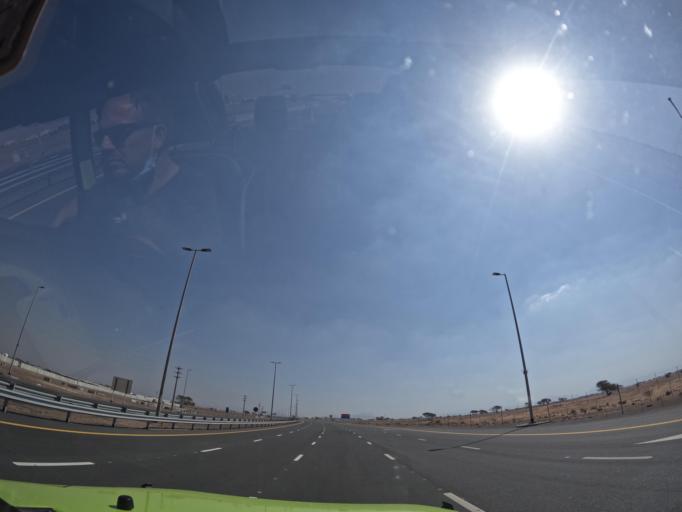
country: AE
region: Ash Shariqah
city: Adh Dhayd
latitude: 24.9112
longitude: 55.7826
